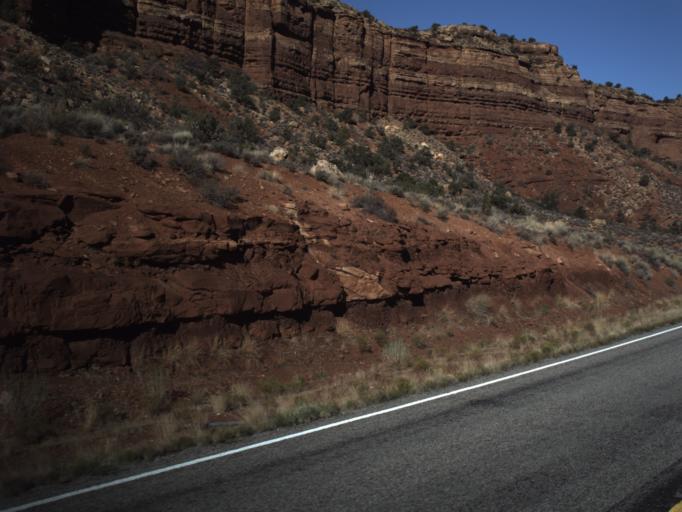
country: US
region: Utah
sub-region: San Juan County
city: Blanding
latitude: 37.7211
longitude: -110.2472
